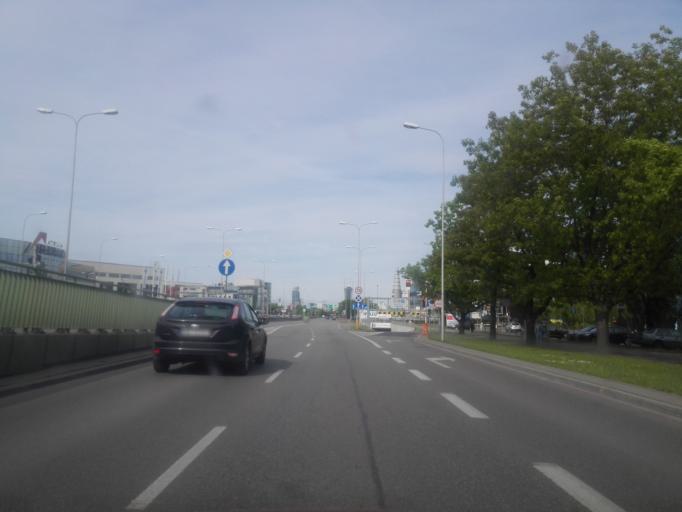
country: PL
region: Masovian Voivodeship
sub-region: Warszawa
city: Wlochy
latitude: 52.2110
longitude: 20.9513
